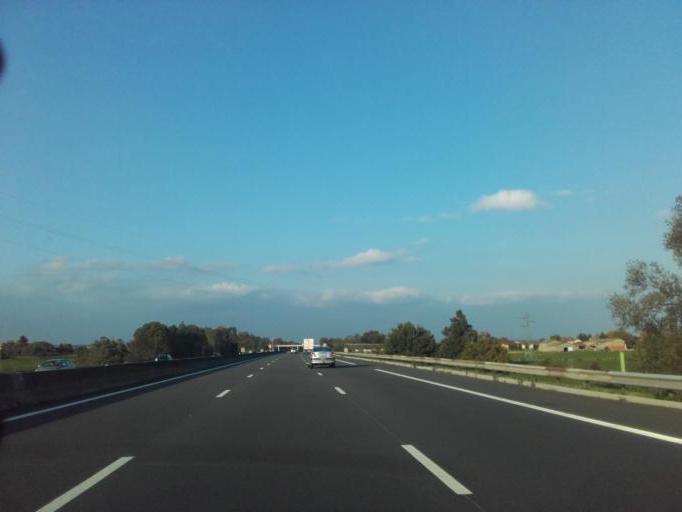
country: FR
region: Rhone-Alpes
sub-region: Departement de l'Ain
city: Pont-de-Vaux
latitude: 46.4605
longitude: 4.8767
